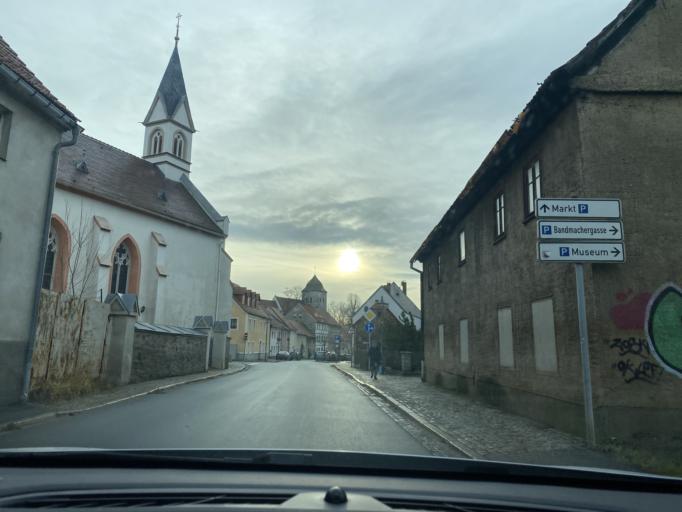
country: DE
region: Saxony
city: Reichenbach
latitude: 51.1437
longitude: 14.8049
